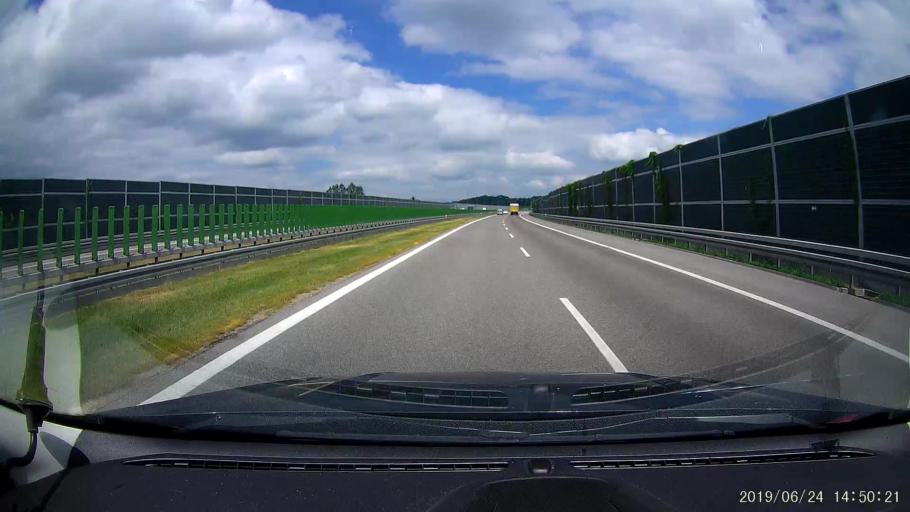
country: PL
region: Subcarpathian Voivodeship
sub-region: Powiat debicki
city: Brzeznica
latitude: 50.0921
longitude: 21.5041
